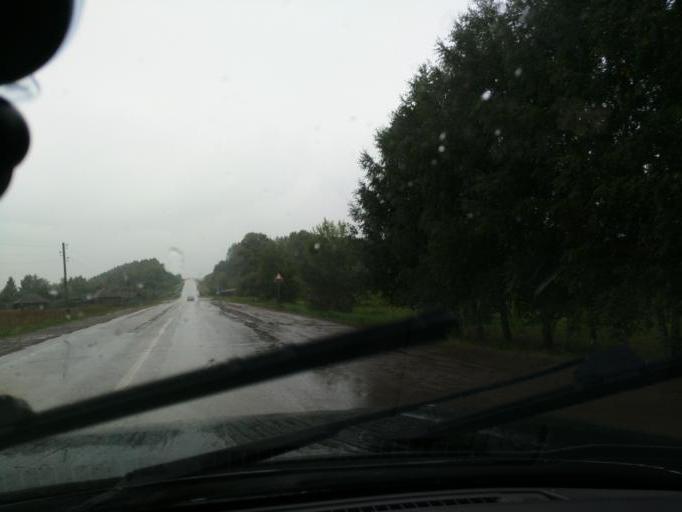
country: RU
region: Perm
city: Osa
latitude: 57.1876
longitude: 55.5909
